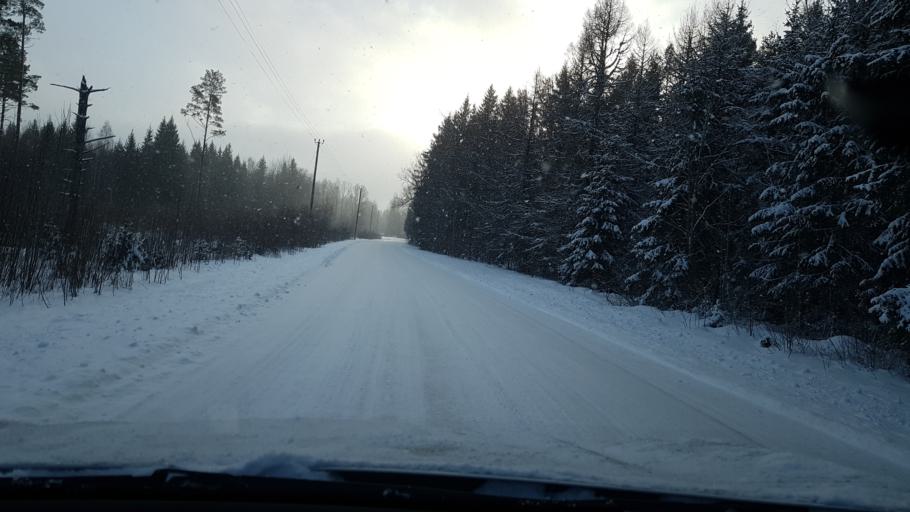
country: EE
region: Harju
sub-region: Nissi vald
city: Turba
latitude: 59.1918
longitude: 24.1397
